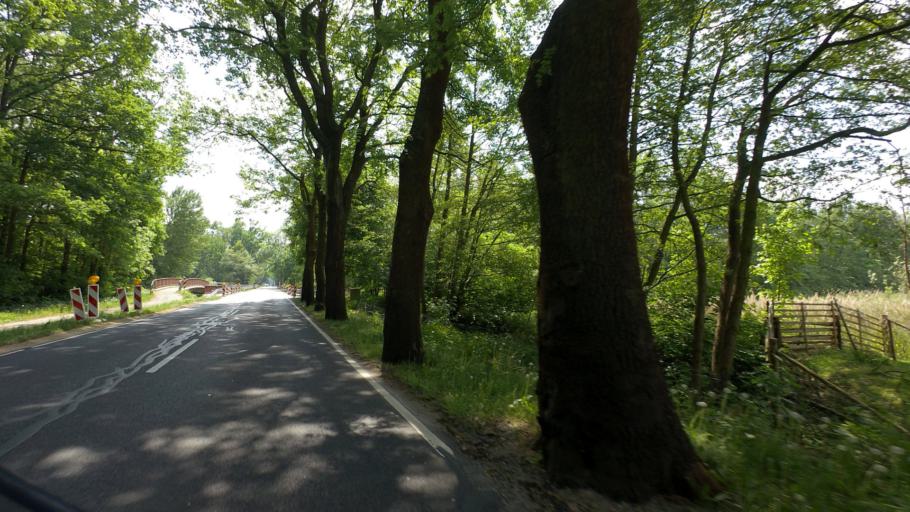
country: DE
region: Saxony
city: Rietschen
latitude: 51.4116
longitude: 14.7879
